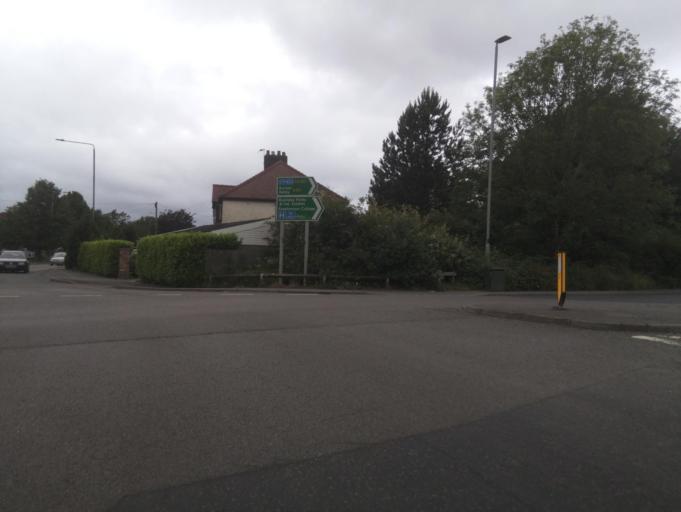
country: GB
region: England
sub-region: Leicestershire
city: Coalville
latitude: 52.7186
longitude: -1.3547
